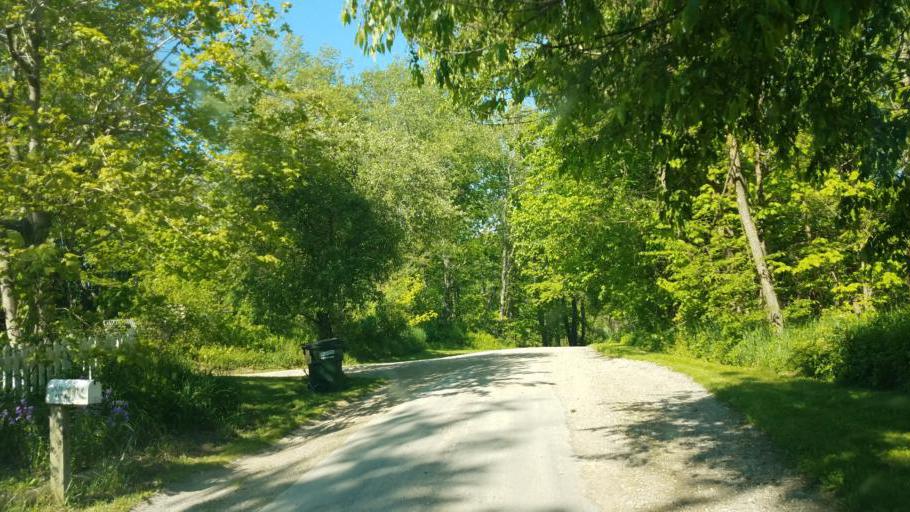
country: US
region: Ohio
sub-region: Belmont County
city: Barnesville
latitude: 40.0714
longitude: -81.3458
